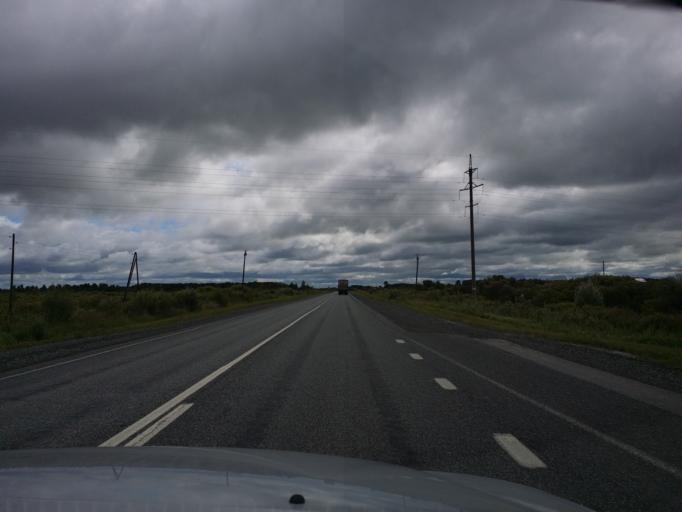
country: RU
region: Tjumen
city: Yarkovo
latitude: 57.2504
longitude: 66.7990
